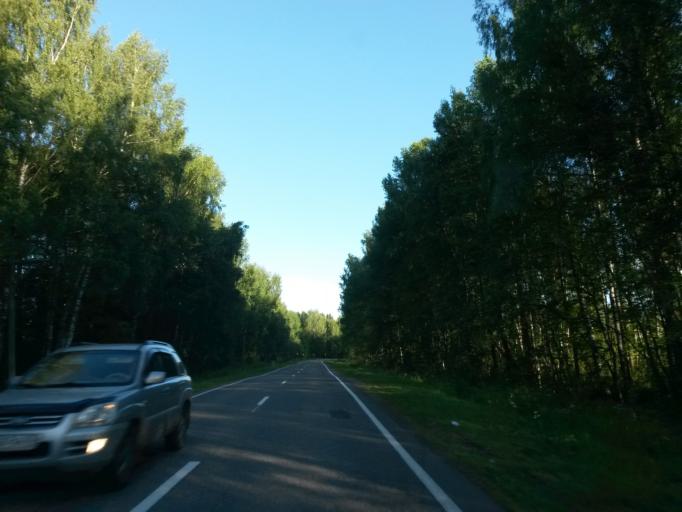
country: RU
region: Jaroslavl
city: Tutayev
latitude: 57.9230
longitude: 39.5107
